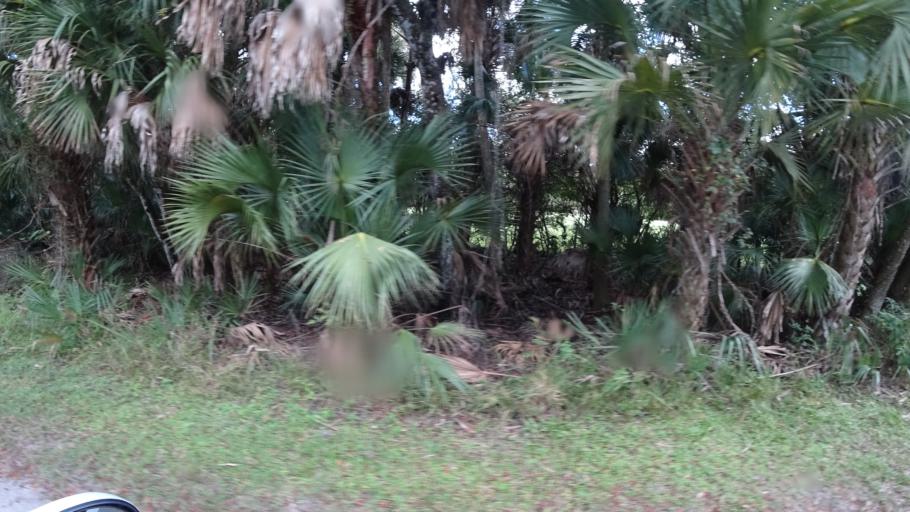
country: US
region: Florida
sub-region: Sarasota County
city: Lake Sarasota
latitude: 27.2439
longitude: -82.3143
